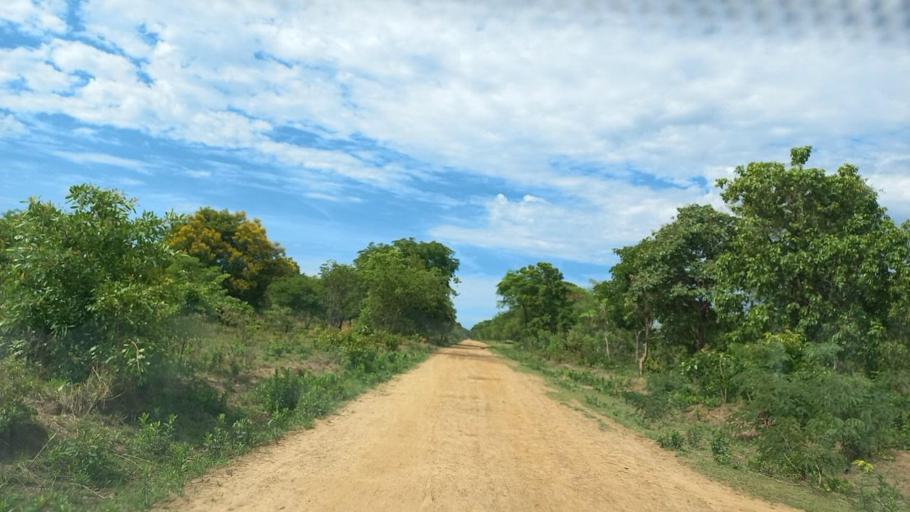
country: ZM
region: North-Western
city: Kabompo
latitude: -13.5218
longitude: 24.3838
